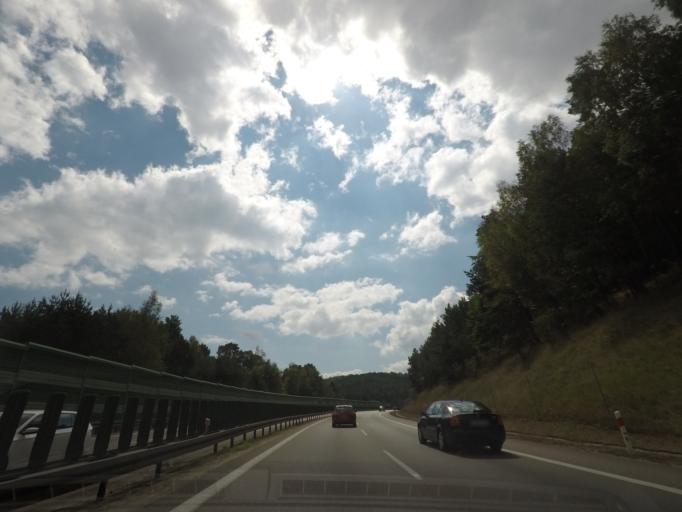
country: PL
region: Pomeranian Voivodeship
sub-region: Gdynia
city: Pogorze
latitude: 54.5260
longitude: 18.4585
